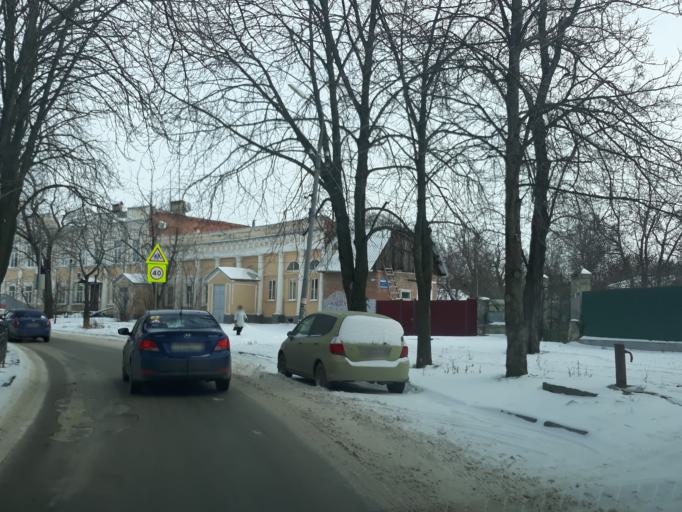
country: RU
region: Rostov
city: Taganrog
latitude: 47.2101
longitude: 38.9213
